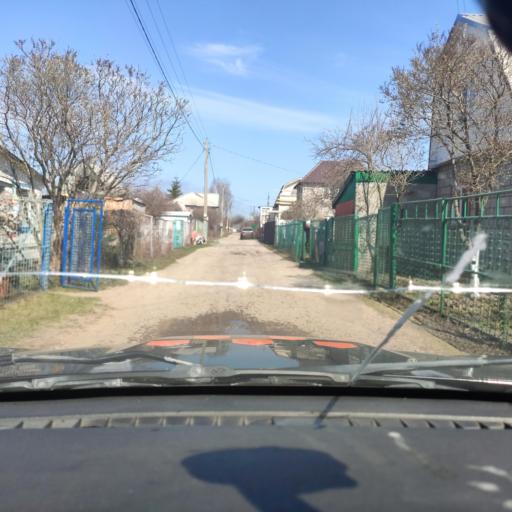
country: RU
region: Samara
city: Tol'yatti
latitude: 53.5844
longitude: 49.3136
